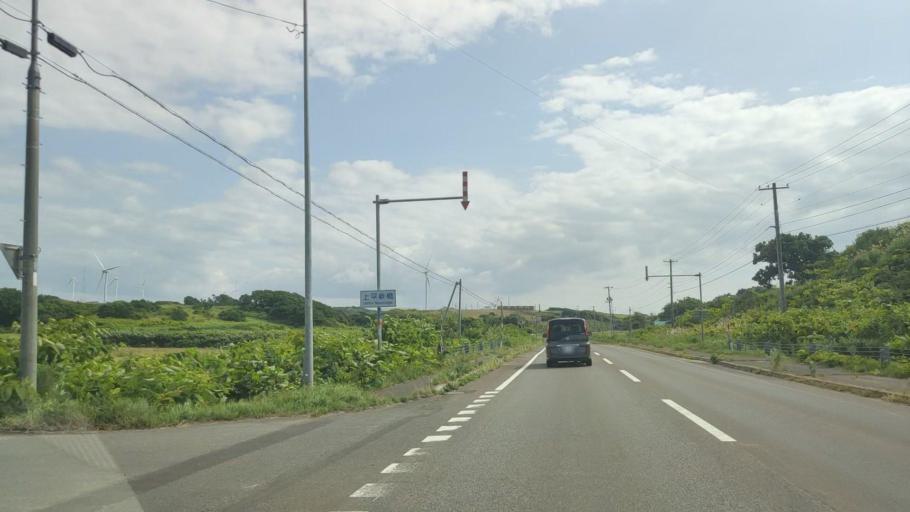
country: JP
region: Hokkaido
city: Rumoi
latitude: 44.2614
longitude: 141.6565
